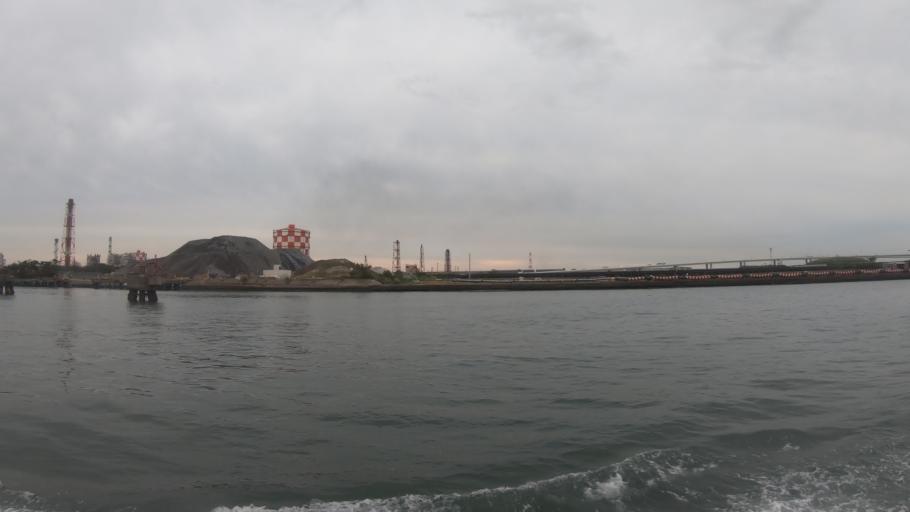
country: JP
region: Kanagawa
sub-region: Kawasaki-shi
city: Kawasaki
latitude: 35.4847
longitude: 139.7084
